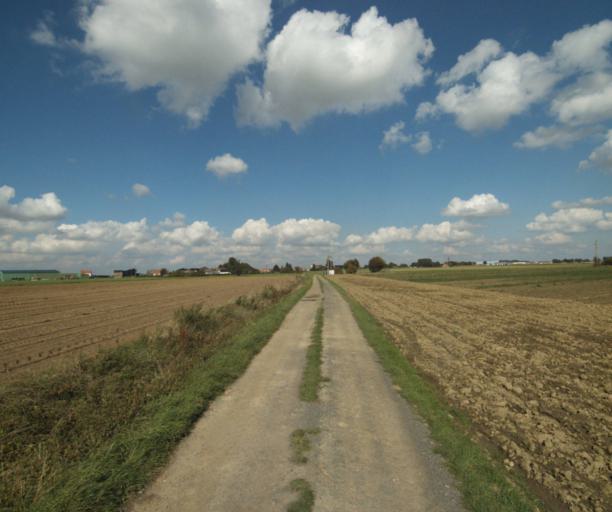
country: FR
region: Nord-Pas-de-Calais
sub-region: Departement du Nord
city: Illies
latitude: 50.5501
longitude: 2.8207
